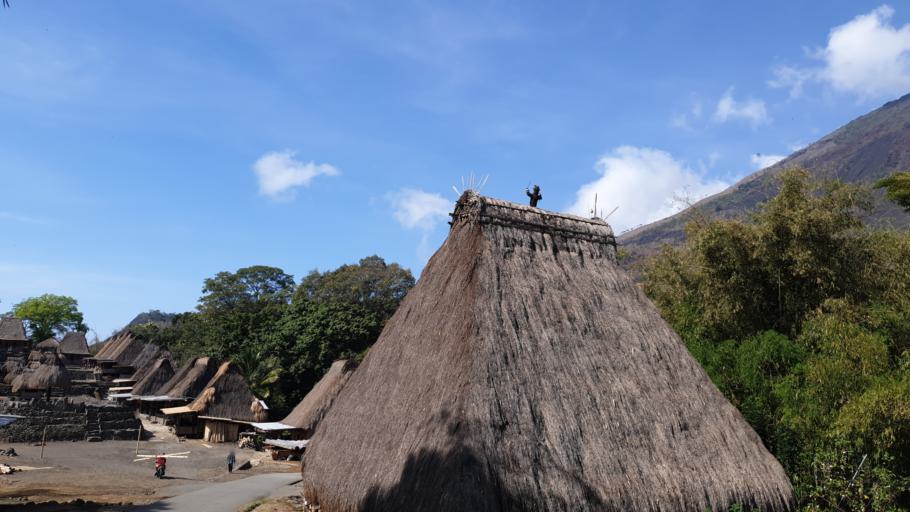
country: ID
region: East Nusa Tenggara
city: Gurusina
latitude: -8.8763
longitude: 120.9862
